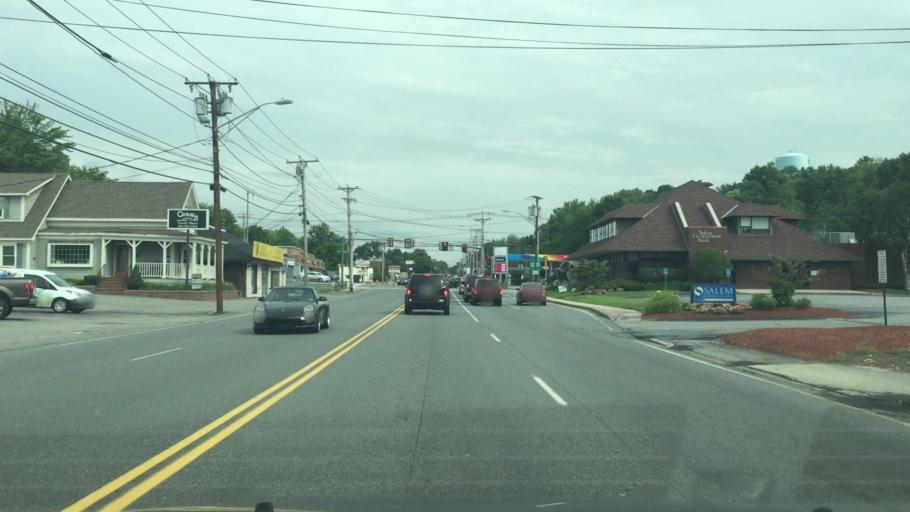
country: US
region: New Hampshire
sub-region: Rockingham County
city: Salem
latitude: 42.7785
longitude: -71.2278
